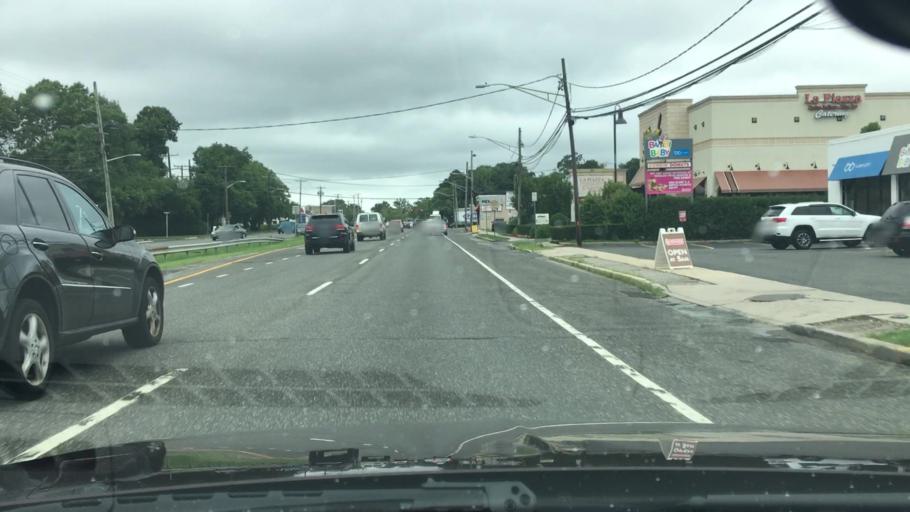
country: US
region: New York
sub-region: Suffolk County
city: South Huntington
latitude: 40.8115
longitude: -73.4095
